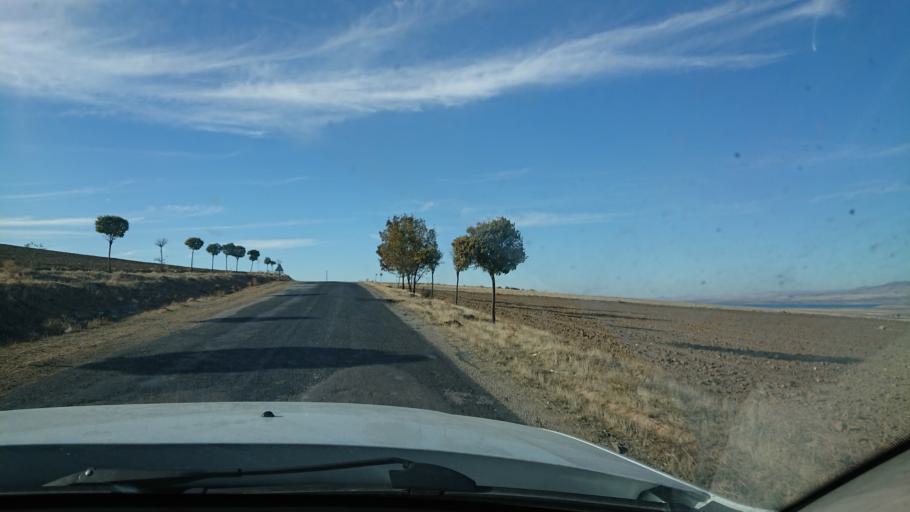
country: TR
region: Aksaray
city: Sariyahsi
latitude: 38.9716
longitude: 33.8651
